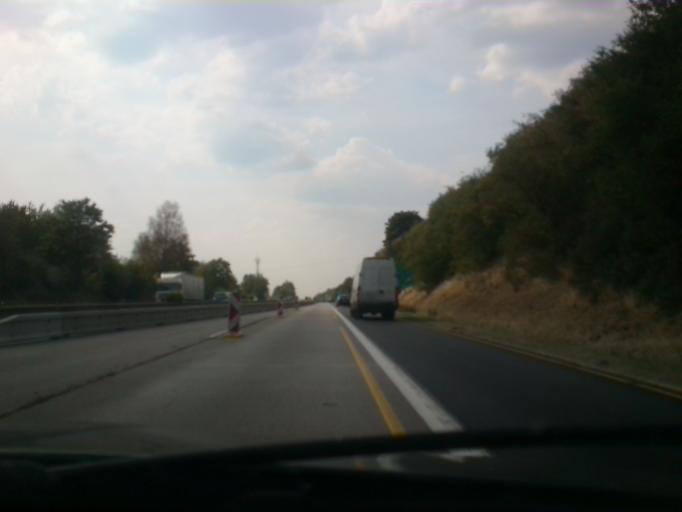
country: CZ
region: Central Bohemia
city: Divisov
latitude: 49.8376
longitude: 14.8352
